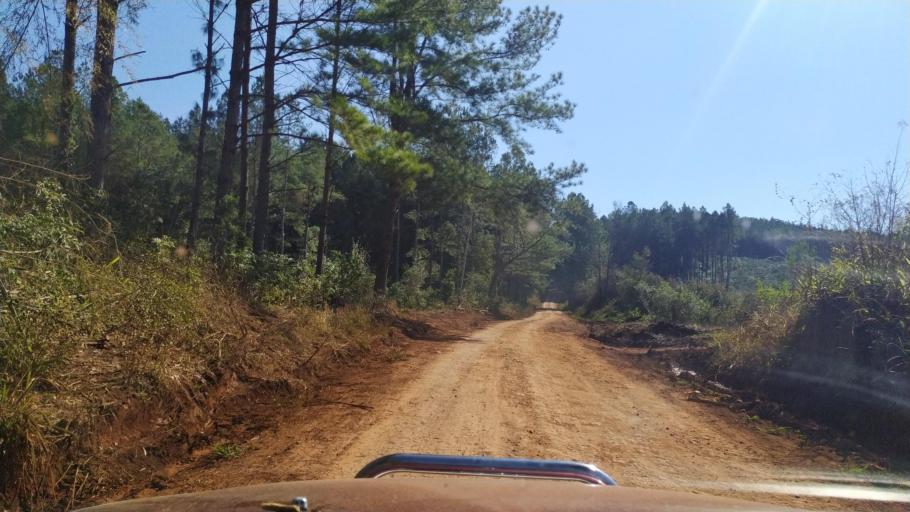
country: AR
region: Misiones
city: El Alcazar
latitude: -26.7315
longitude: -54.6761
